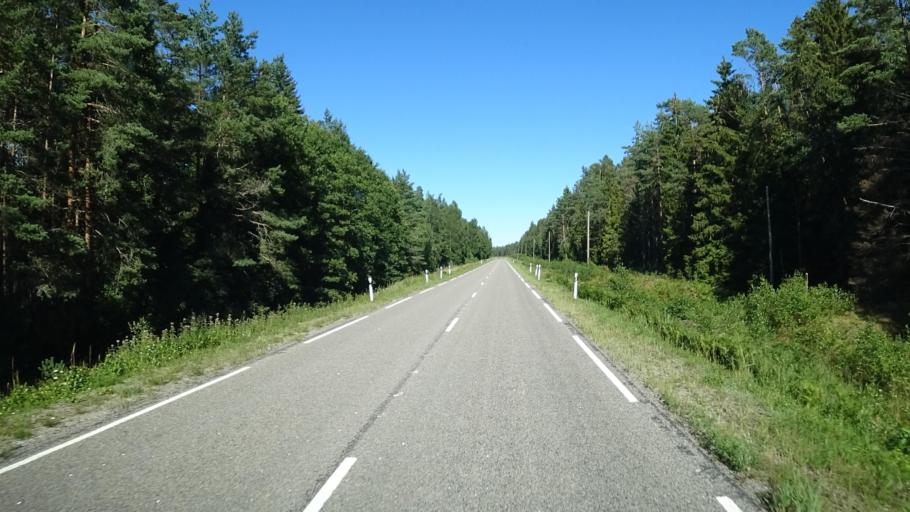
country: LV
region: Dundaga
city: Dundaga
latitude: 57.6883
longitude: 22.3765
